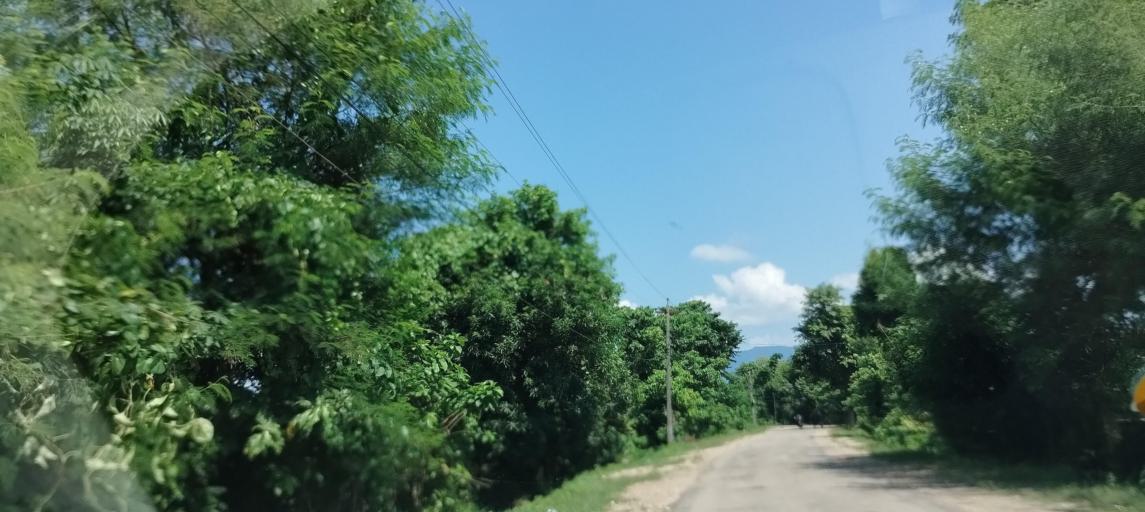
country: NP
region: Far Western
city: Tikapur
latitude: 28.5039
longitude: 81.3023
